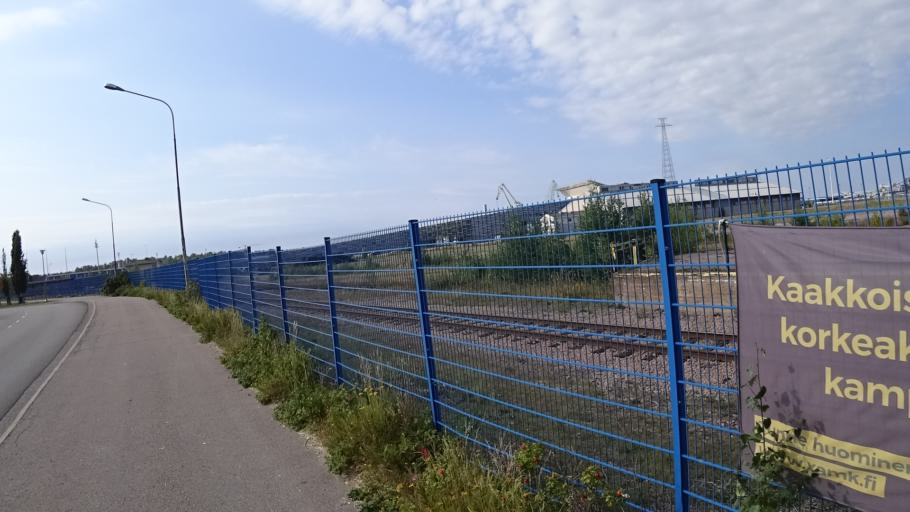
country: FI
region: Kymenlaakso
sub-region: Kotka-Hamina
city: Kotka
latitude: 60.4705
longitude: 26.9484
